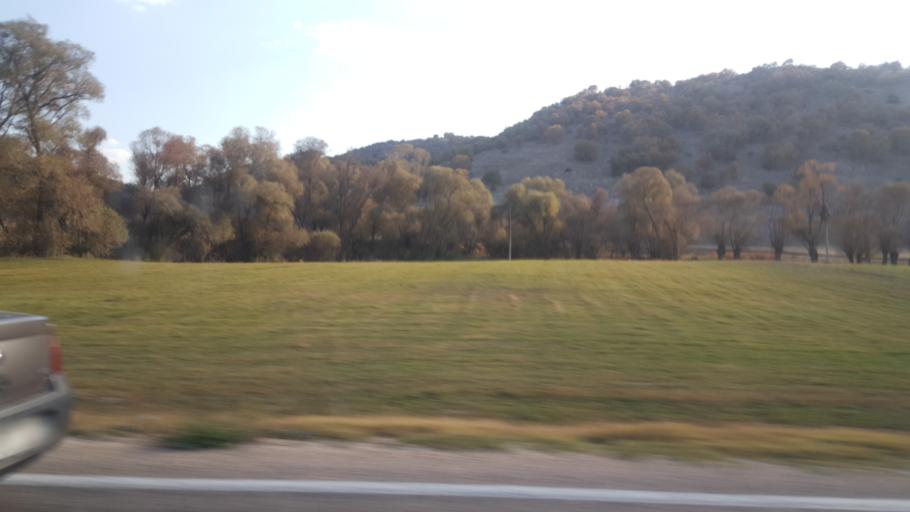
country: TR
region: Eskisehir
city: Kirka
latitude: 39.3572
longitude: 30.5913
